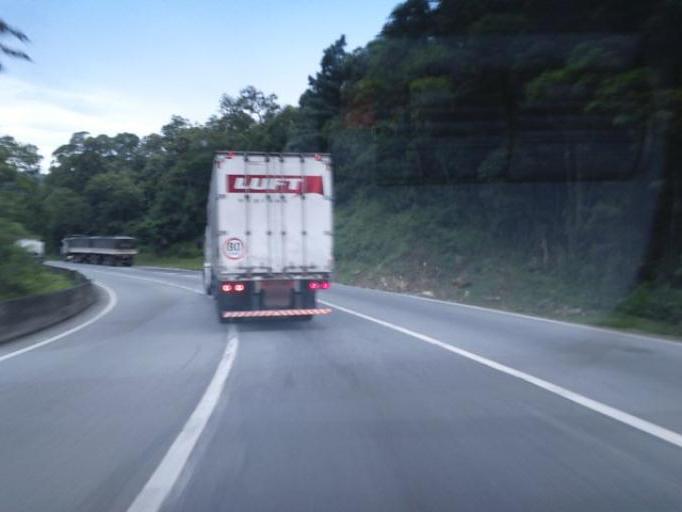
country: BR
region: Parana
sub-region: Guaratuba
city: Guaratuba
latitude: -25.8637
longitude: -48.9508
